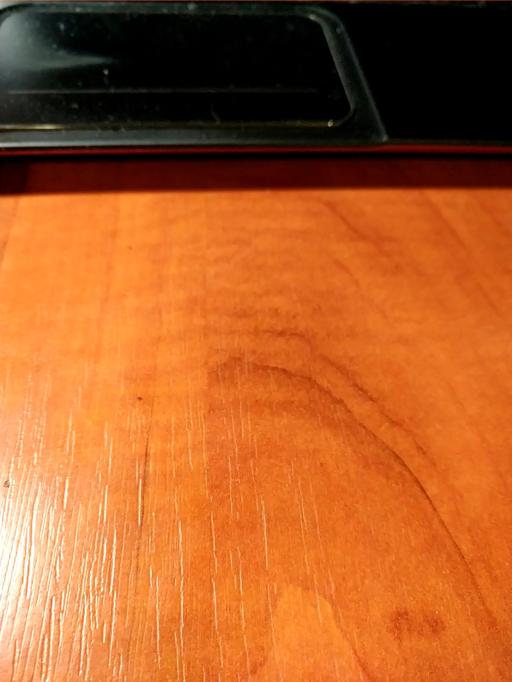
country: RU
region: Lipetsk
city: Chaplygin
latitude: 53.3443
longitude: 40.0483
